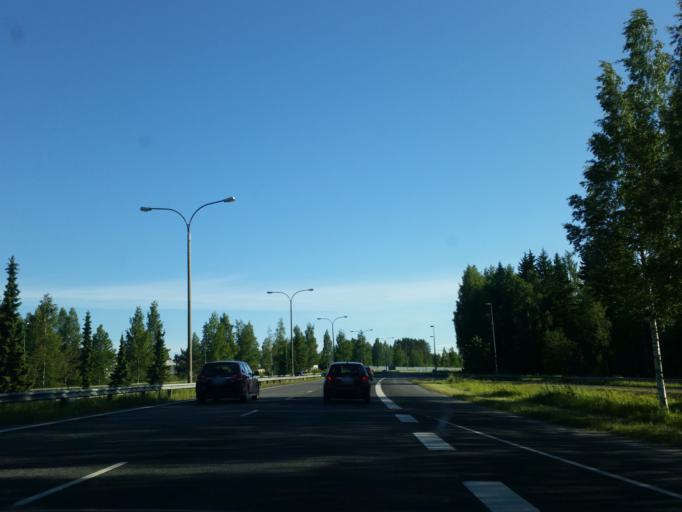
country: FI
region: Northern Savo
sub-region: Kuopio
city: Kuopio
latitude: 62.8825
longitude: 27.6340
